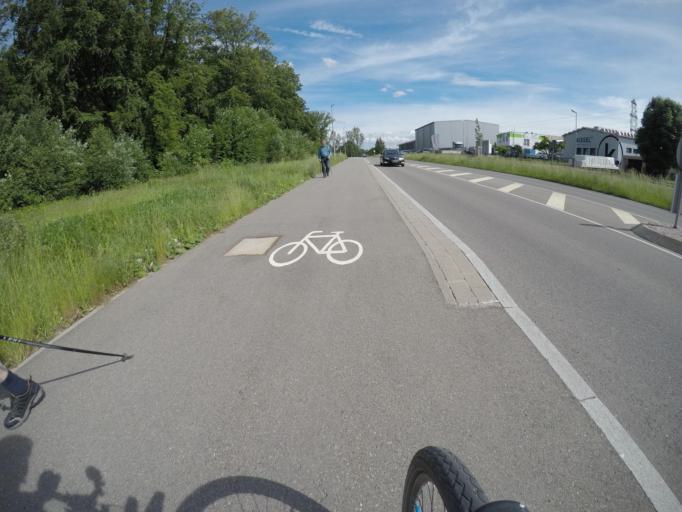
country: DE
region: Baden-Wuerttemberg
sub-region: Regierungsbezirk Stuttgart
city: Ehningen
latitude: 48.6656
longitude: 8.9551
